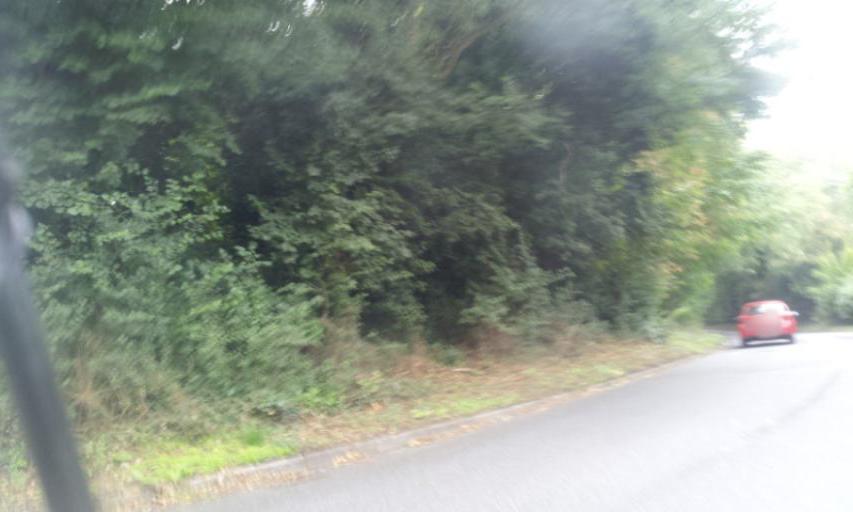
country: GB
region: England
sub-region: Kent
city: Larkfield
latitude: 51.2958
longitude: 0.4300
